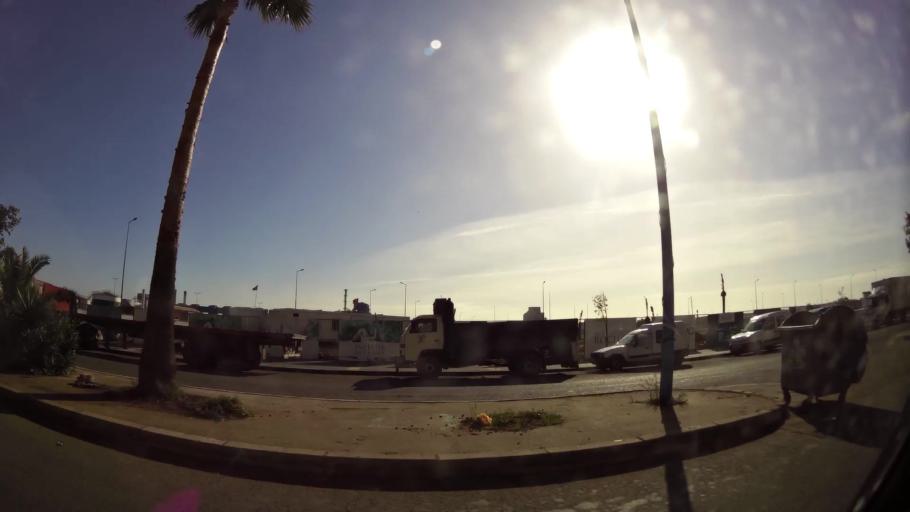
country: MA
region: Grand Casablanca
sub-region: Casablanca
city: Casablanca
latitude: 33.6000
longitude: -7.5778
